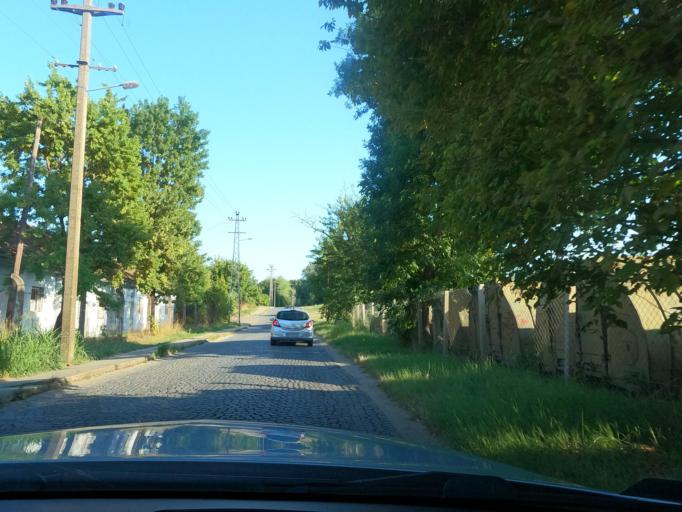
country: RS
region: Autonomna Pokrajina Vojvodina
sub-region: Juznobacki Okrug
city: Novi Sad
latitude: 45.2333
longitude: 19.8266
